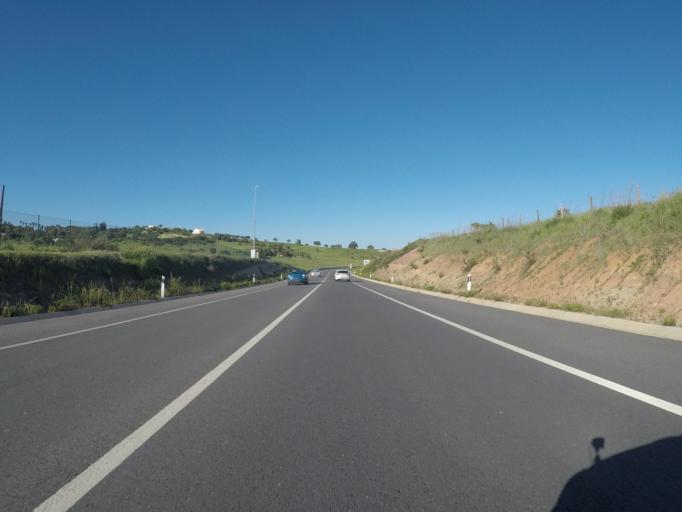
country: PT
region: Faro
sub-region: Lagos
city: Lagos
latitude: 37.1096
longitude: -8.6940
